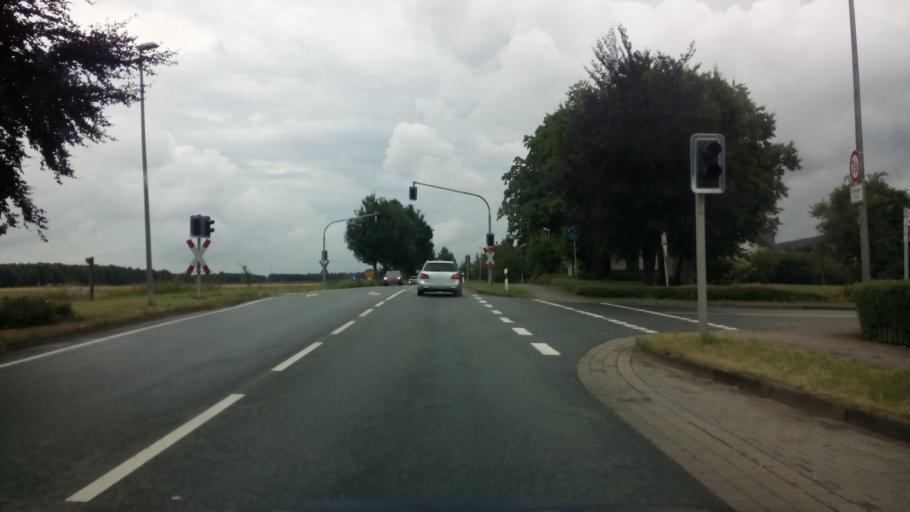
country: DE
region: Lower Saxony
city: Bad Essen
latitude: 52.3318
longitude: 8.3157
